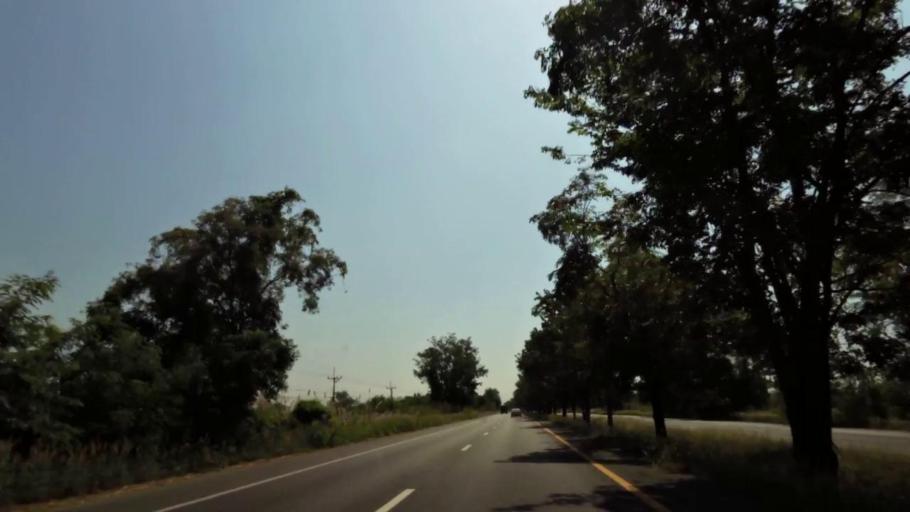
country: TH
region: Nakhon Sawan
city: Kao Liao
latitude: 15.9271
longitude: 100.1122
